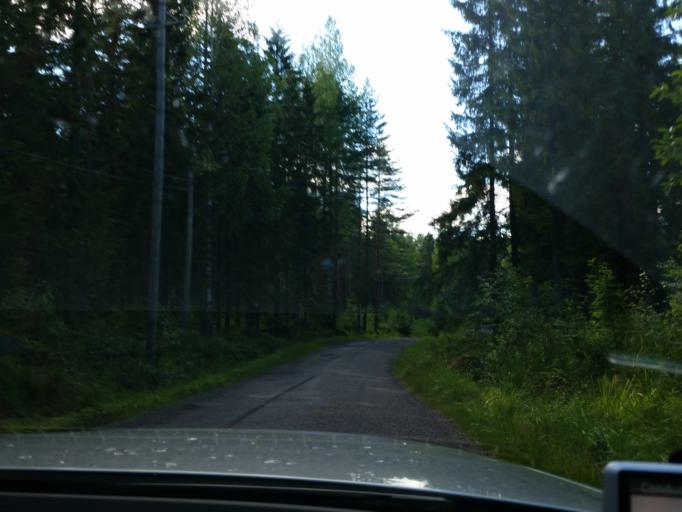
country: FI
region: Uusimaa
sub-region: Helsinki
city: Kaerkoelae
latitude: 60.5546
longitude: 23.9901
